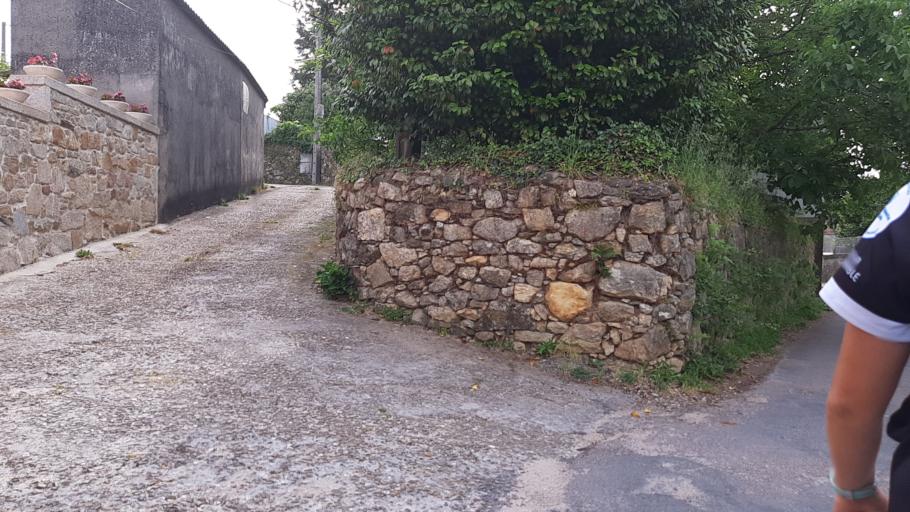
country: ES
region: Galicia
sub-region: Provincia de Pontevedra
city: O Rosal
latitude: 41.9296
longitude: -8.8334
